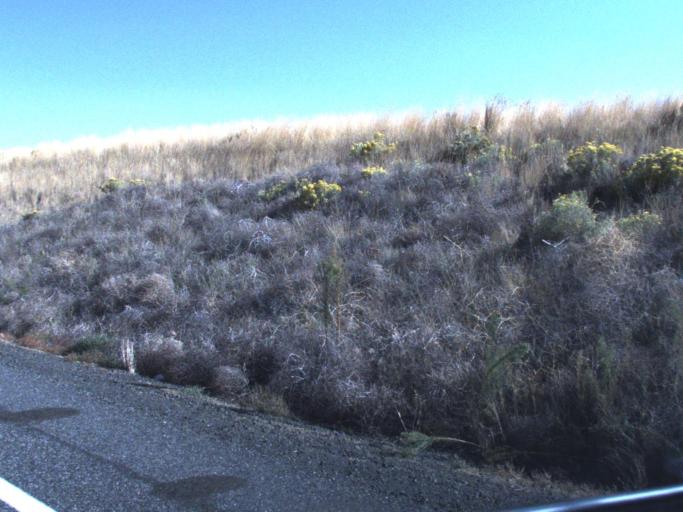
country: US
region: Washington
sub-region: Benton County
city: Highland
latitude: 46.1542
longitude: -119.1499
